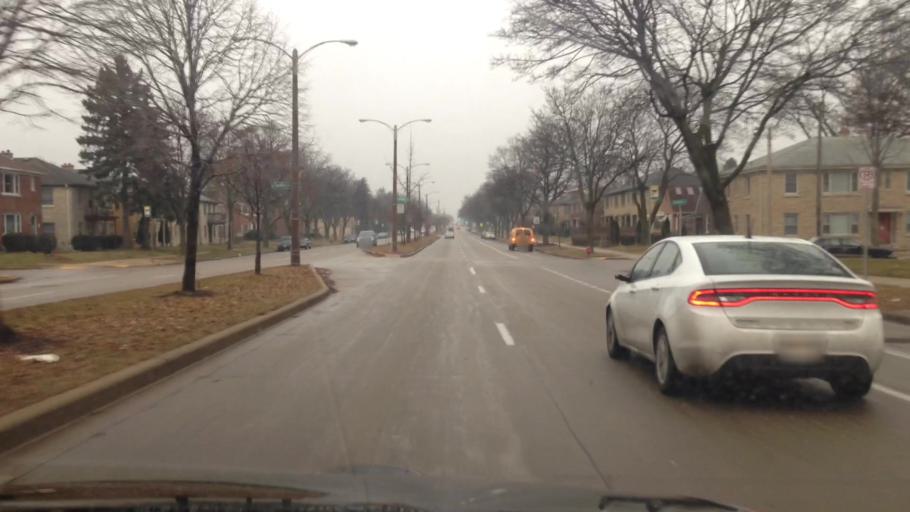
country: US
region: Wisconsin
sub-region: Milwaukee County
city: Wauwatosa
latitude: 43.0694
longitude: -88.0073
